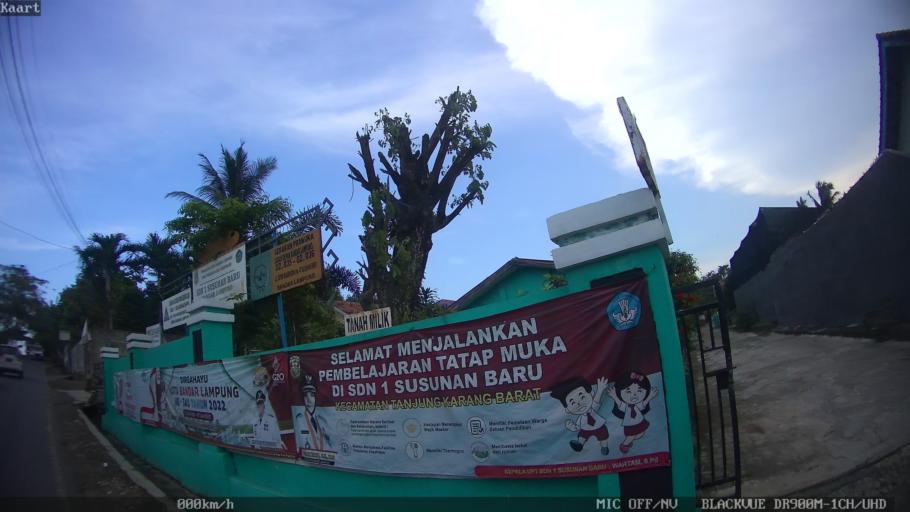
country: ID
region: Lampung
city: Kedaton
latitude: -5.4017
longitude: 105.2331
